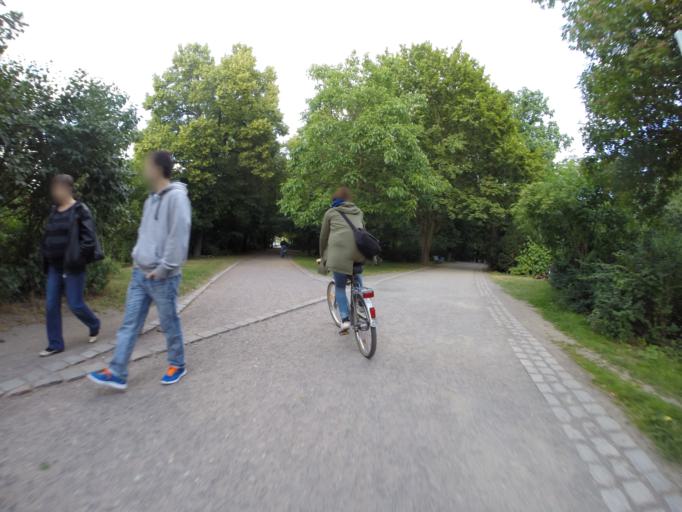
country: DE
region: Berlin
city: Berlin Schoeneberg
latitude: 52.4817
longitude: 13.3357
